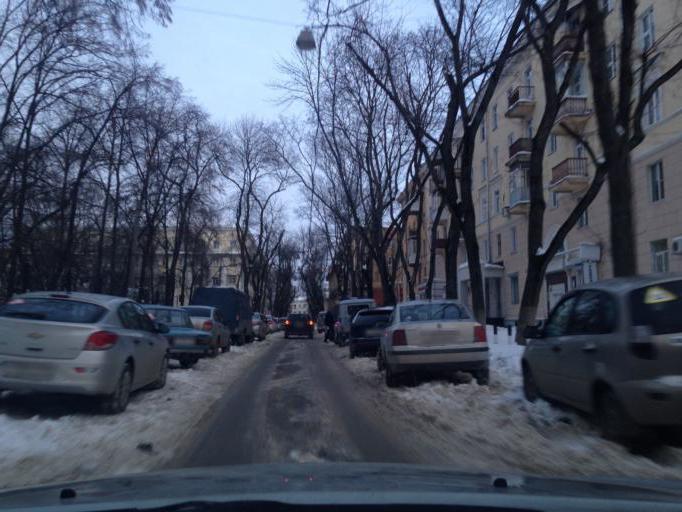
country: RU
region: Voronezj
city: Voronezh
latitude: 51.6739
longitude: 39.2061
